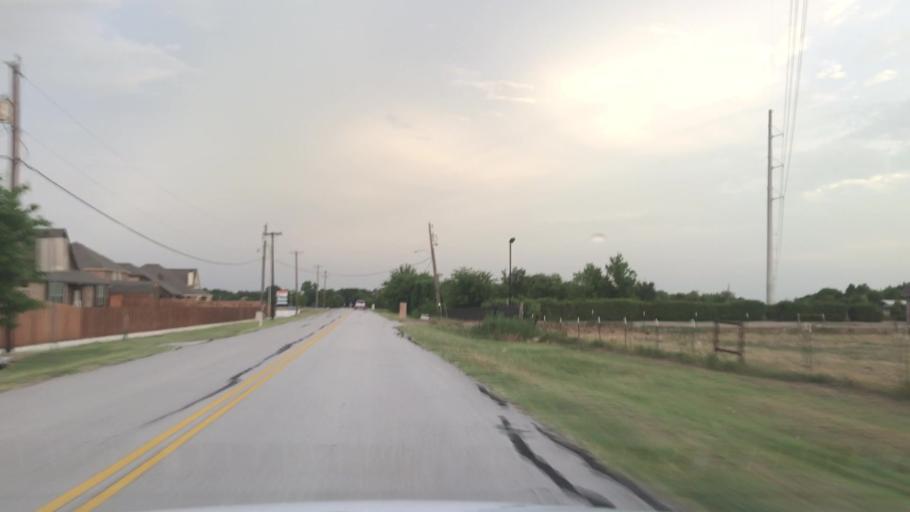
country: US
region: Texas
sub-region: Dallas County
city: Seagoville
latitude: 32.6970
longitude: -96.5583
